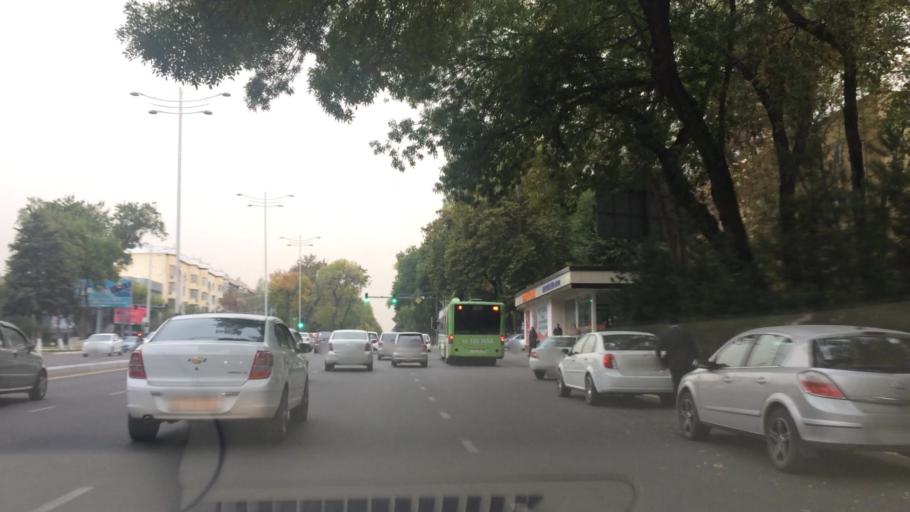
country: UZ
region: Toshkent Shahri
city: Tashkent
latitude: 41.3073
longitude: 69.2936
